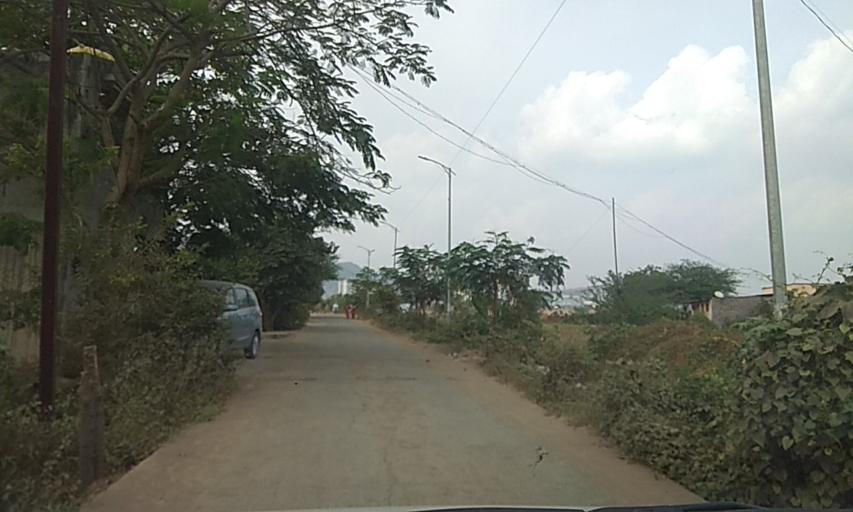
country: IN
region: Maharashtra
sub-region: Pune Division
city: Pimpri
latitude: 18.5785
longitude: 73.7083
